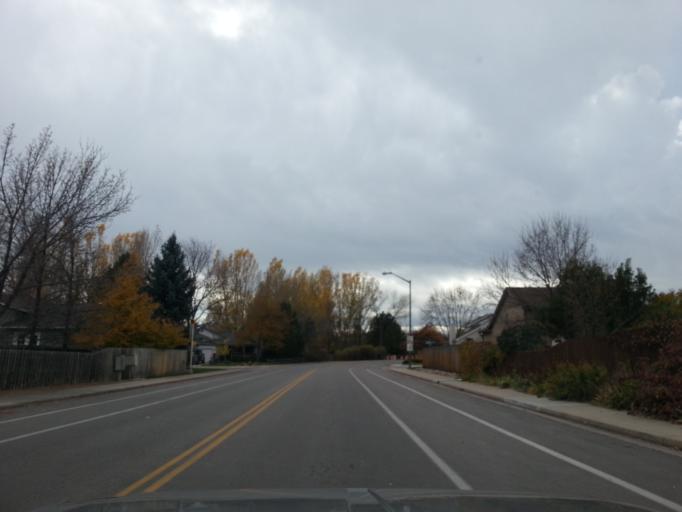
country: US
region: Colorado
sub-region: Larimer County
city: Fort Collins
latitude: 40.5318
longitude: -105.0335
